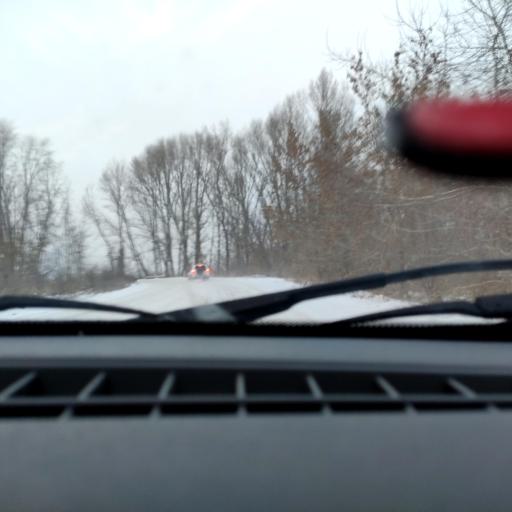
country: RU
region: Bashkortostan
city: Blagoveshchensk
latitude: 54.9099
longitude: 56.0066
